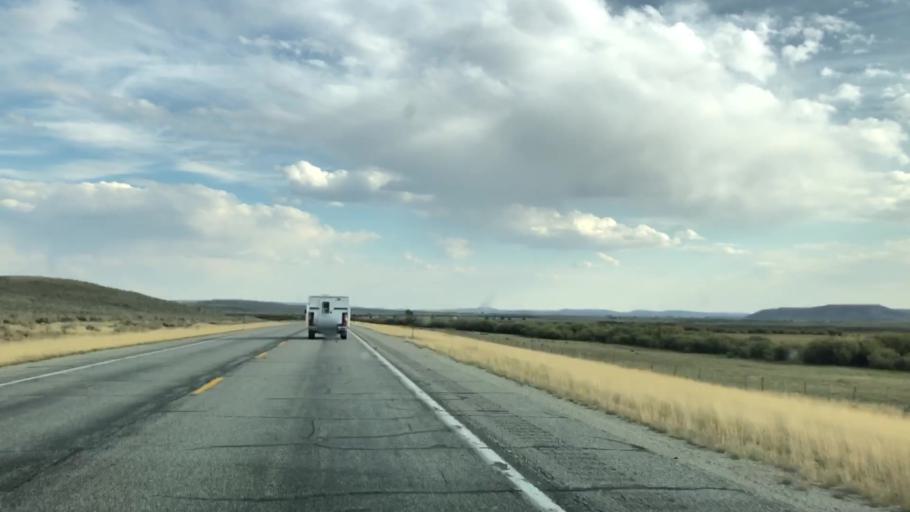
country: US
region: Wyoming
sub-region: Sublette County
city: Pinedale
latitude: 43.0253
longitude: -110.1244
